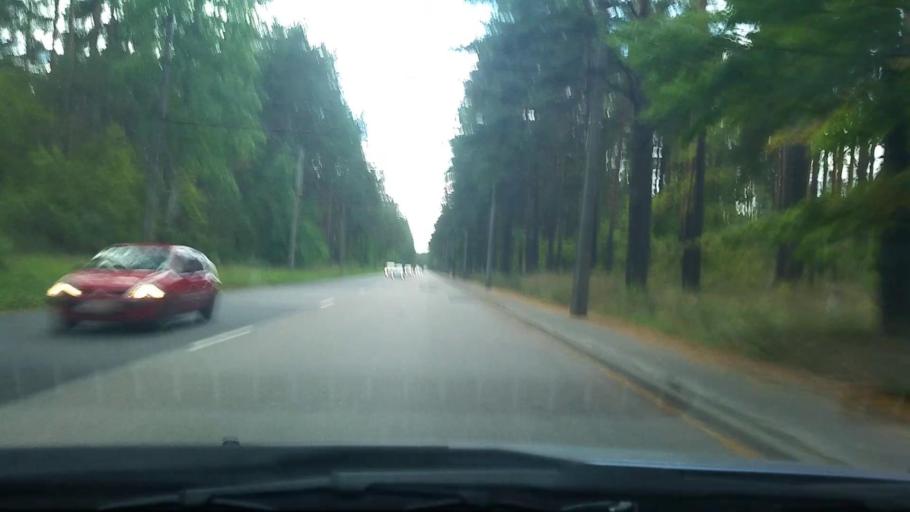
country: LV
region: Stopini
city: Ulbroka
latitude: 56.9628
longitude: 24.2182
